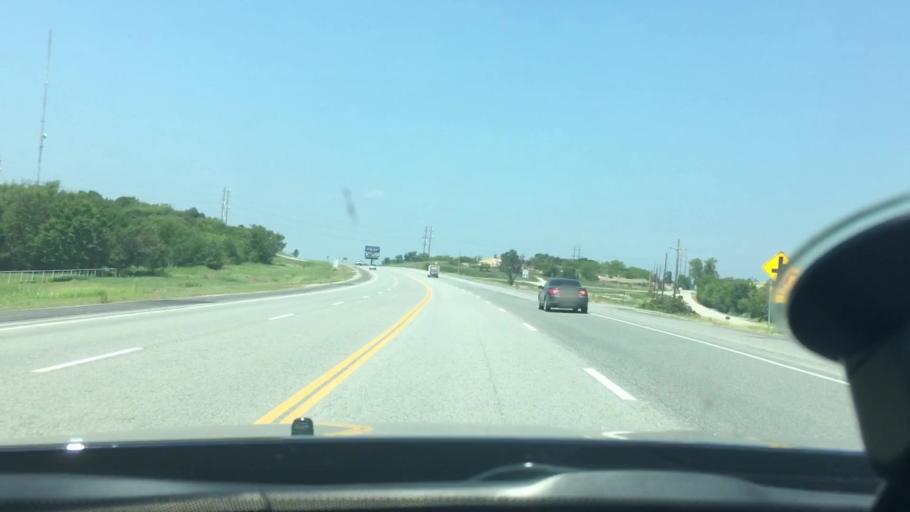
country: US
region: Oklahoma
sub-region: Atoka County
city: Atoka
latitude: 34.3711
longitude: -96.1069
